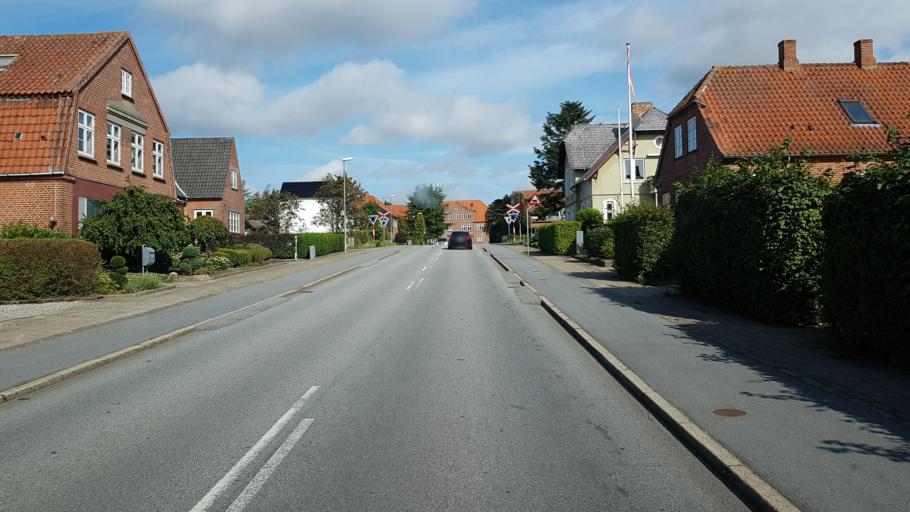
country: DK
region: South Denmark
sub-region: Haderslev Kommune
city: Haderslev
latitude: 55.2501
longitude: 9.4689
